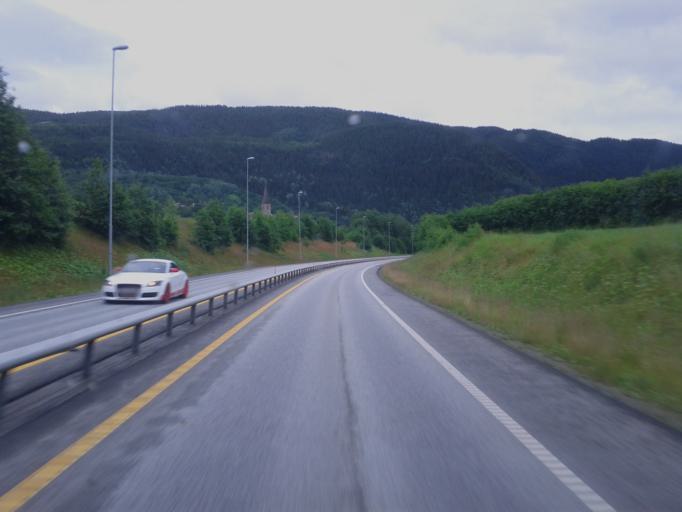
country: NO
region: Sor-Trondelag
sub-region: Melhus
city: Melhus
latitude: 63.2774
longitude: 10.2831
